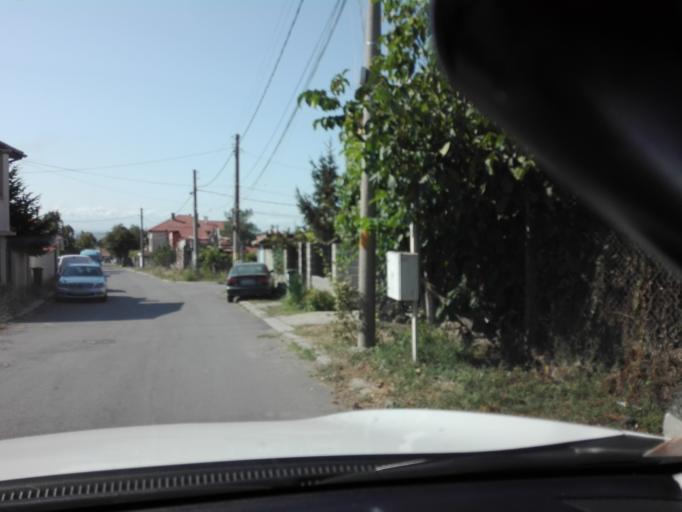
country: BG
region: Burgas
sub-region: Obshtina Kameno
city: Kameno
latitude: 42.6301
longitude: 27.3950
